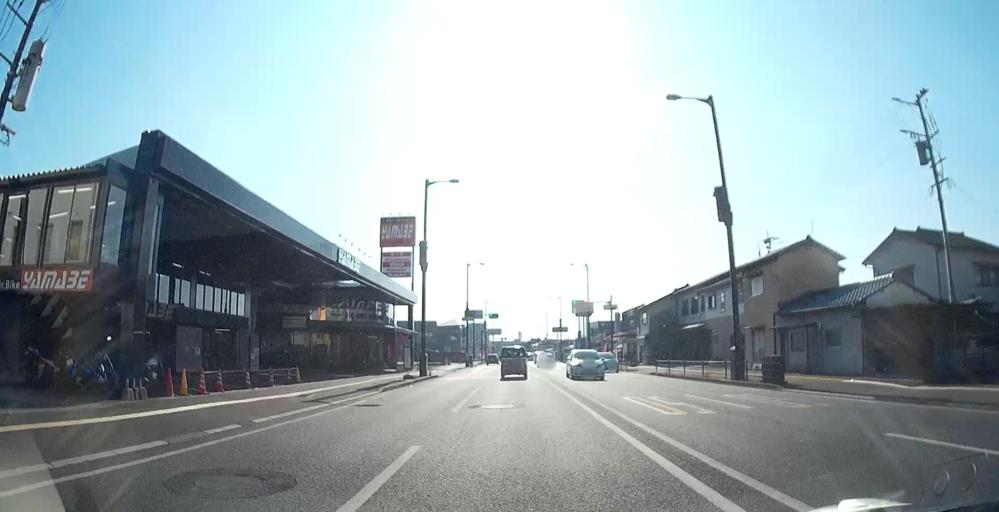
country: JP
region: Kumamoto
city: Kumamoto
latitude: 32.7660
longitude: 130.6912
